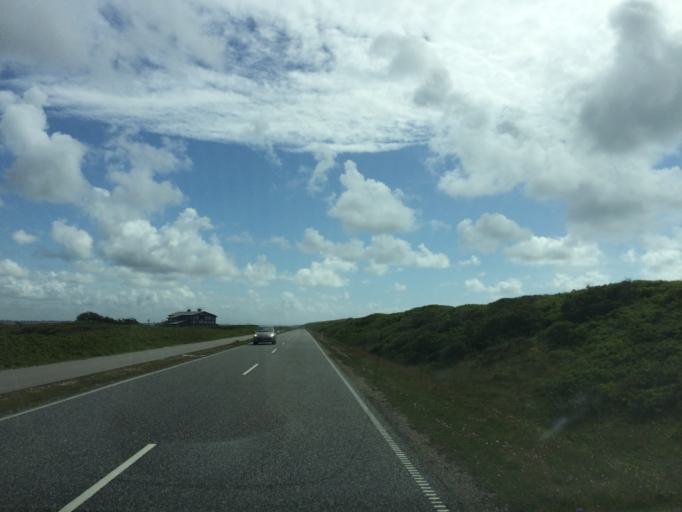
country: DK
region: Central Jutland
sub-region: Holstebro Kommune
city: Ulfborg
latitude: 56.3646
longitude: 8.1226
